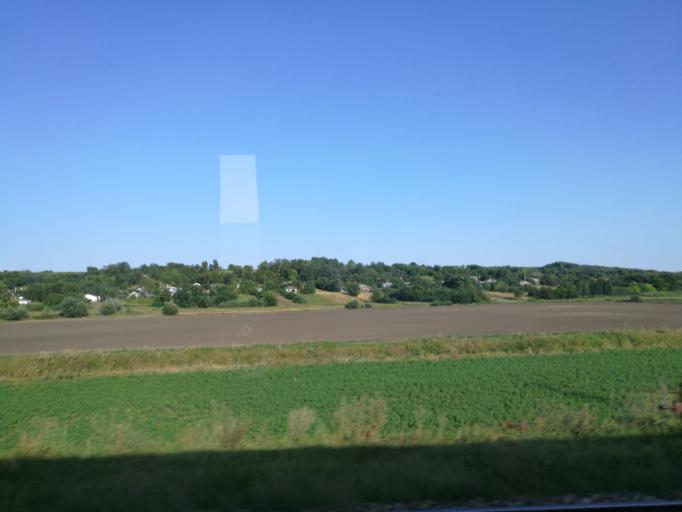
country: RO
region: Vaslui
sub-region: Comuna Albesti
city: Albesti
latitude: 46.4982
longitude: 27.8248
